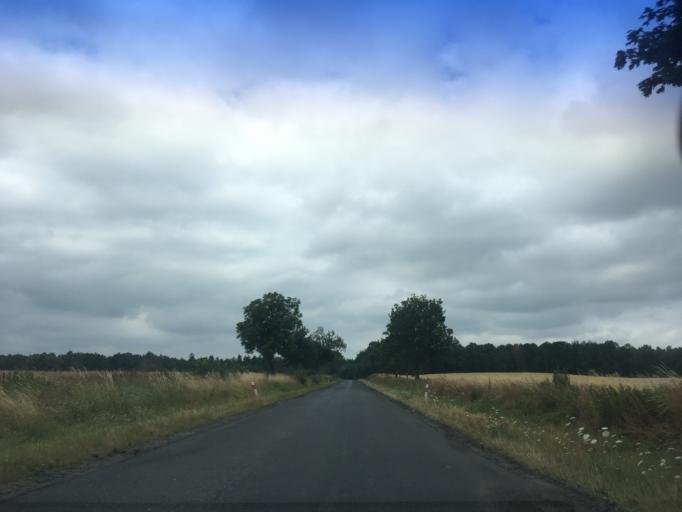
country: PL
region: Lower Silesian Voivodeship
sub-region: Powiat zgorzelecki
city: Sulikow
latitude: 51.0724
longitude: 15.0370
